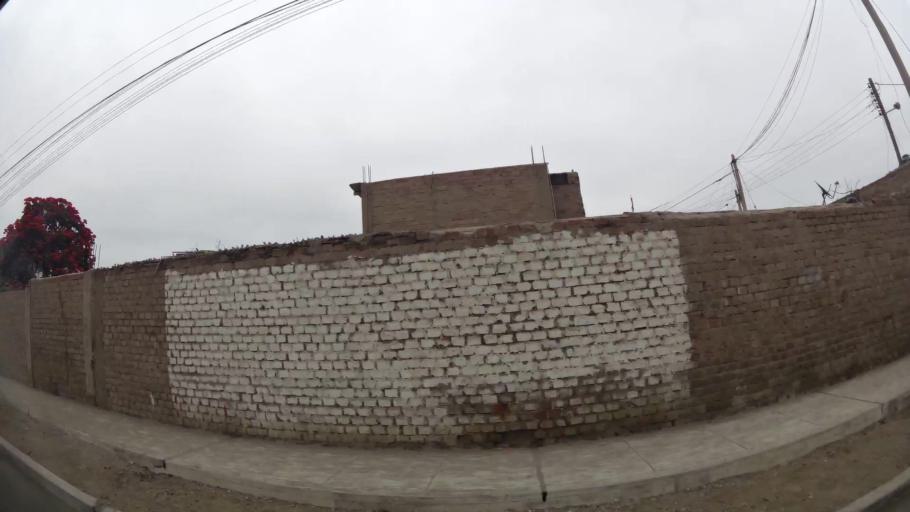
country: PE
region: Ica
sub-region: Provincia de Pisco
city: Pisco
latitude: -13.7118
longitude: -76.1966
